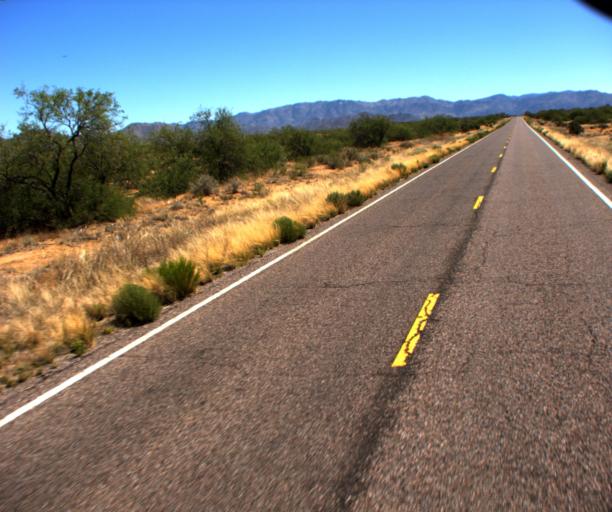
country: US
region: Arizona
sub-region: Yavapai County
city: Congress
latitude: 34.1343
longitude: -112.9231
